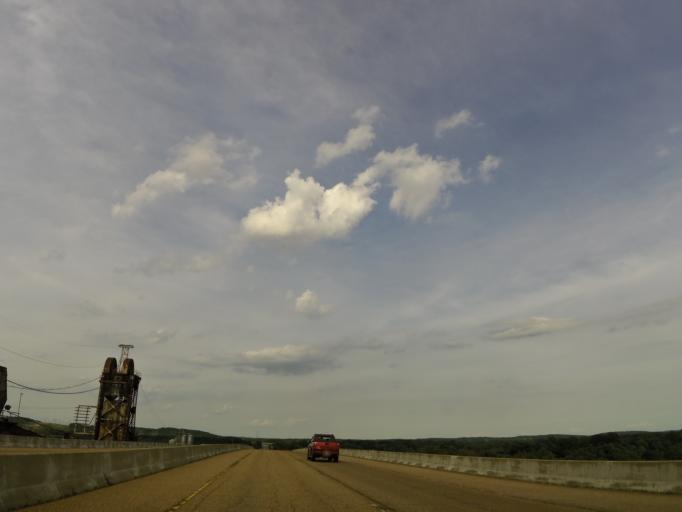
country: US
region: Tennessee
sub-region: Humphreys County
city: New Johnsonville
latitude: 36.0173
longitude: -88.0011
